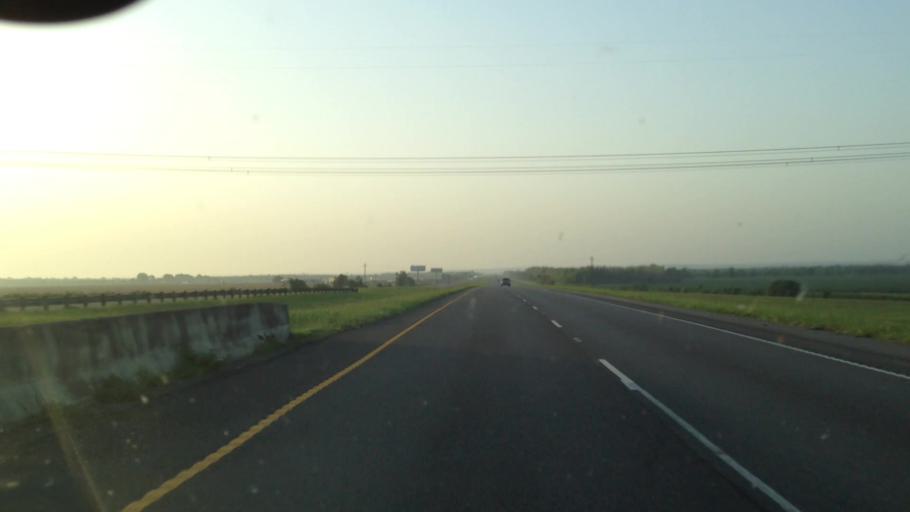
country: US
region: Louisiana
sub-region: Natchitoches Parish
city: Campti
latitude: 31.8381
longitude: -93.2768
